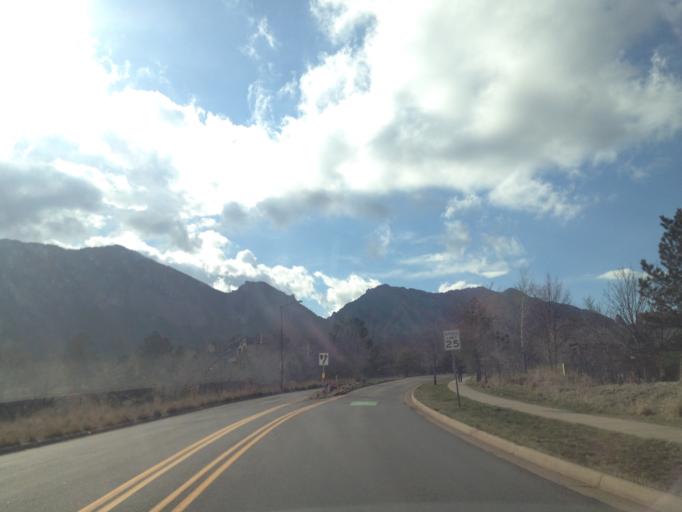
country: US
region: Colorado
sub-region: Boulder County
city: Boulder
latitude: 39.9645
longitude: -105.2526
